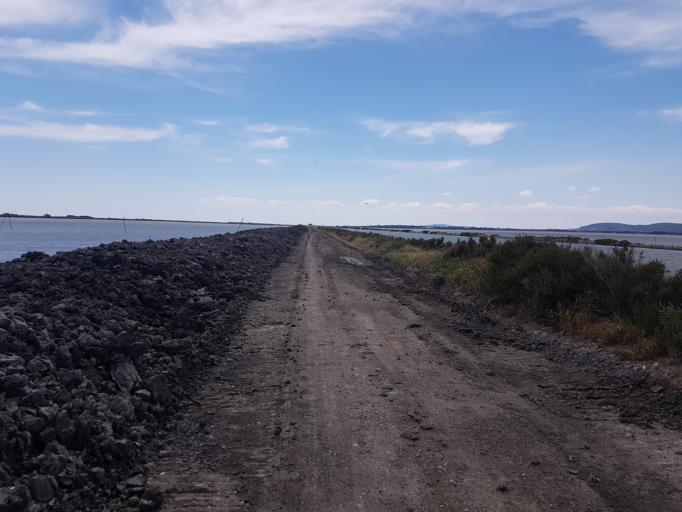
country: FR
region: Languedoc-Roussillon
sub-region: Departement de l'Herault
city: Villeneuve-les-Maguelone
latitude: 43.4911
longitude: 3.8471
